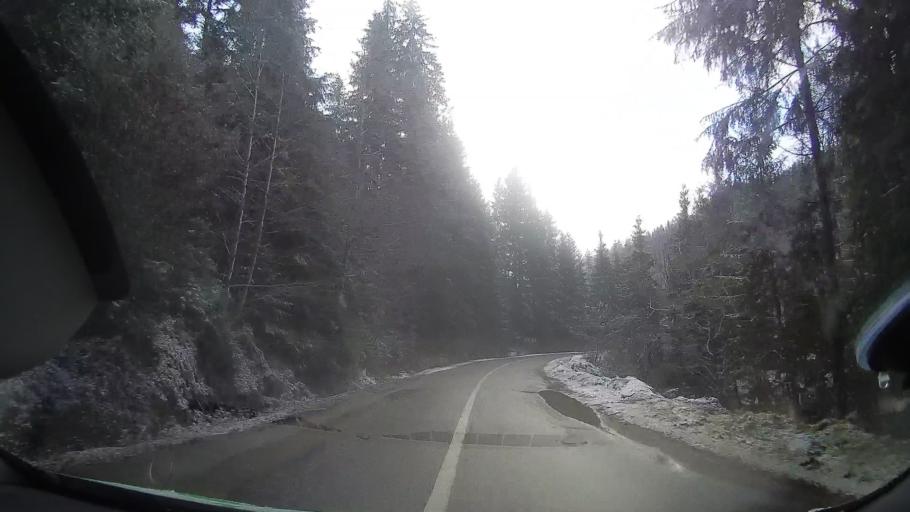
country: RO
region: Alba
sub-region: Comuna Horea
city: Horea
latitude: 46.4885
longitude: 22.9617
